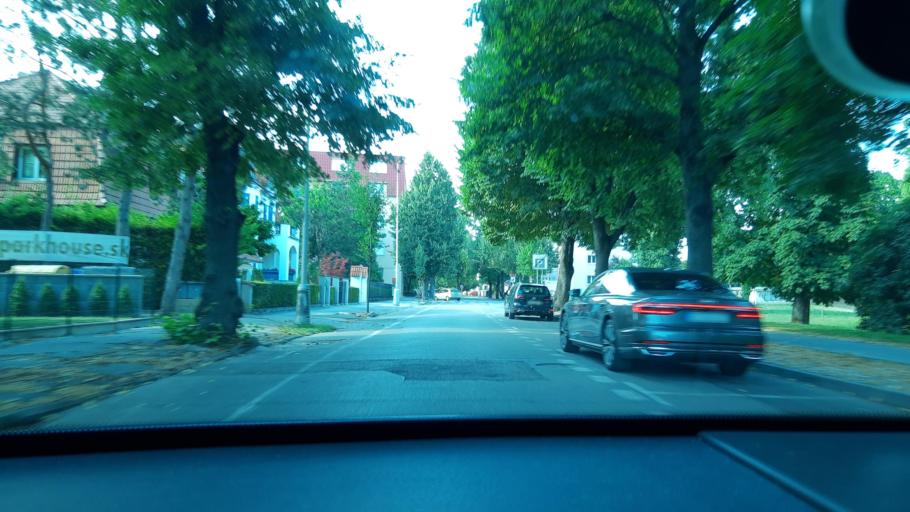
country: SK
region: Trnavsky
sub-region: Okres Trnava
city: Piestany
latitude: 48.5947
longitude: 17.8342
